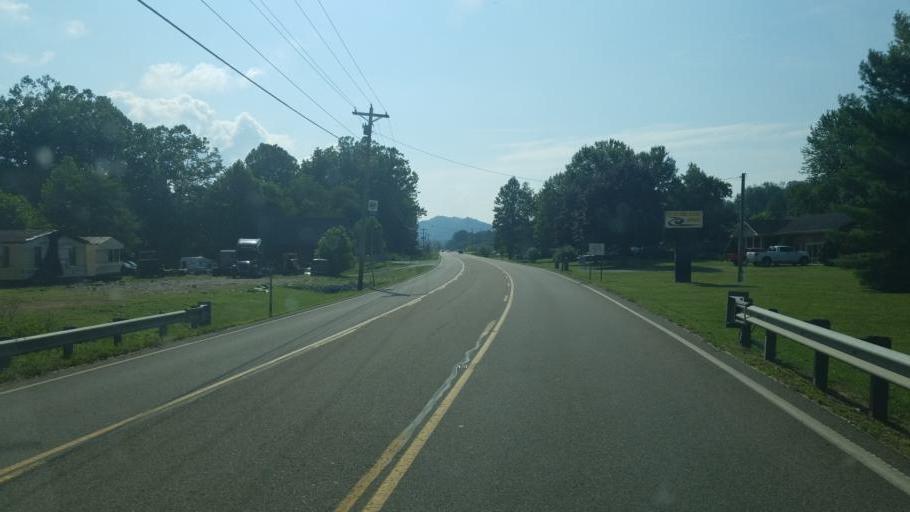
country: US
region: Tennessee
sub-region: Carter County
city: Roan Mountain
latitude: 36.1952
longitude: -82.0630
